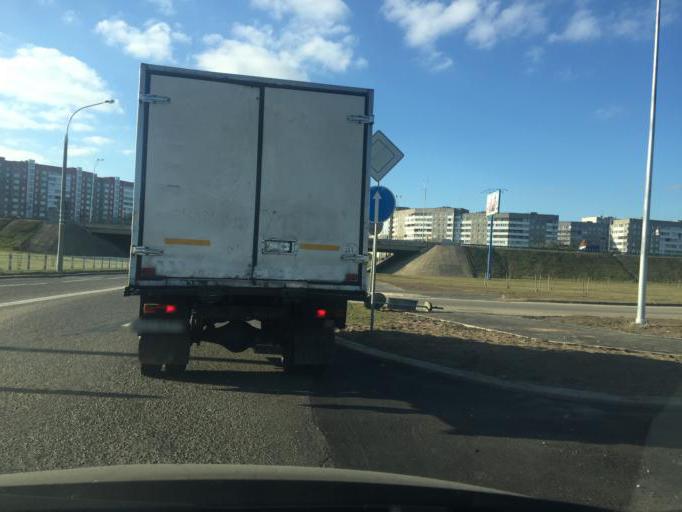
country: BY
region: Minsk
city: Vyaliki Trastsyanets
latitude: 53.8683
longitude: 27.6926
